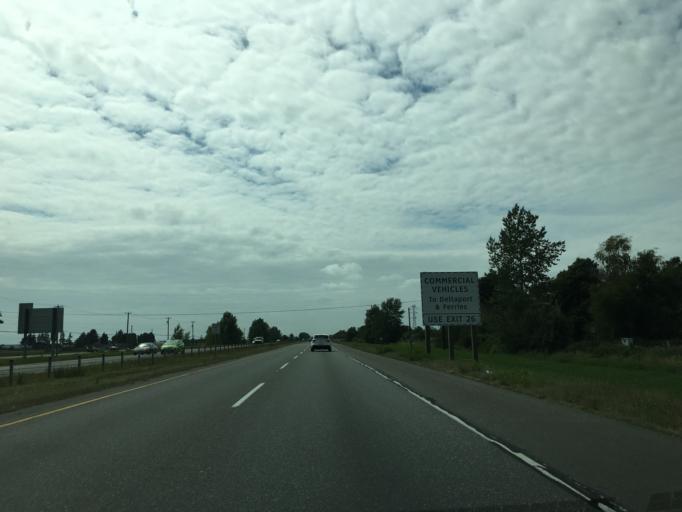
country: CA
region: British Columbia
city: Delta
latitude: 49.0905
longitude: -122.9697
